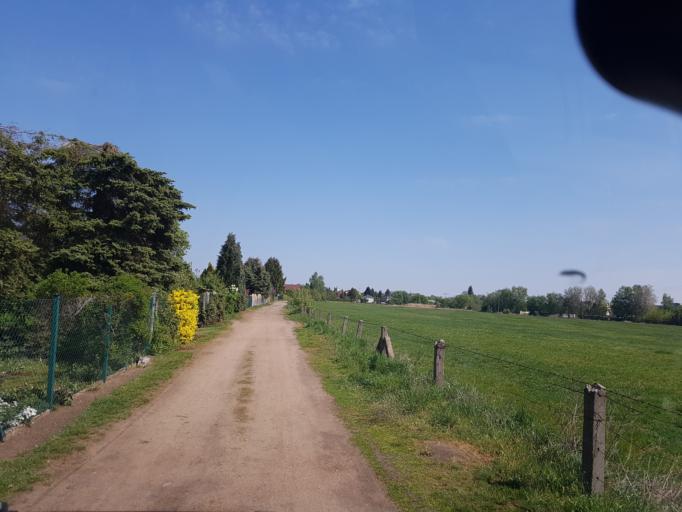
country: DE
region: Brandenburg
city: Finsterwalde
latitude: 51.6201
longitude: 13.6984
